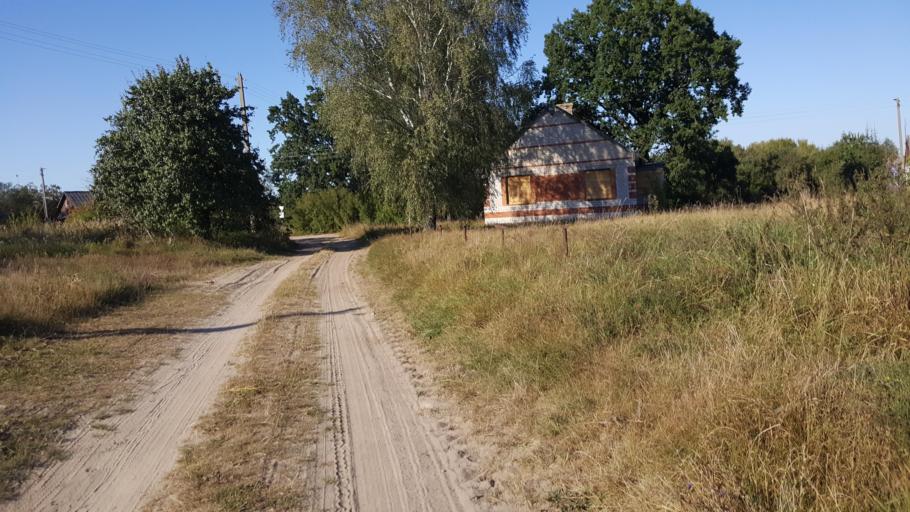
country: BY
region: Brest
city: Vysokaye
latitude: 52.3222
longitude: 23.2625
